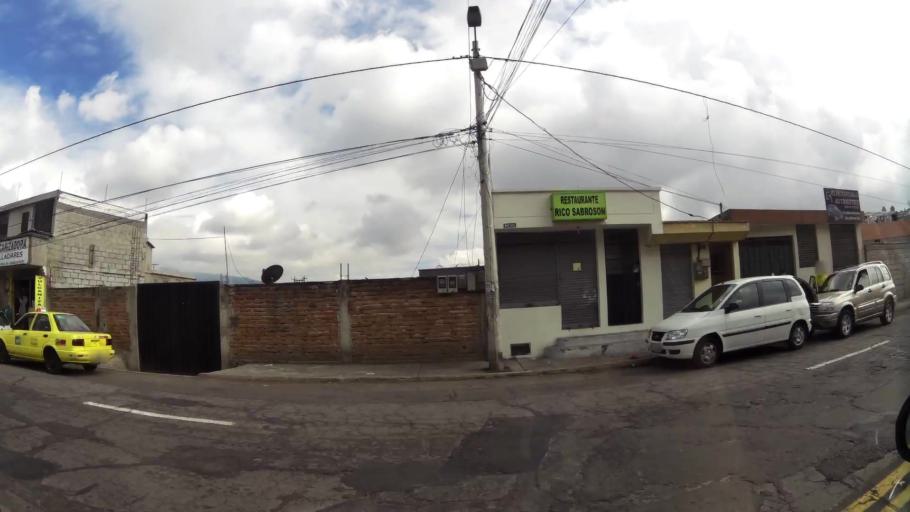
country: EC
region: Pichincha
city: Quito
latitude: -0.1542
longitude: -78.4679
